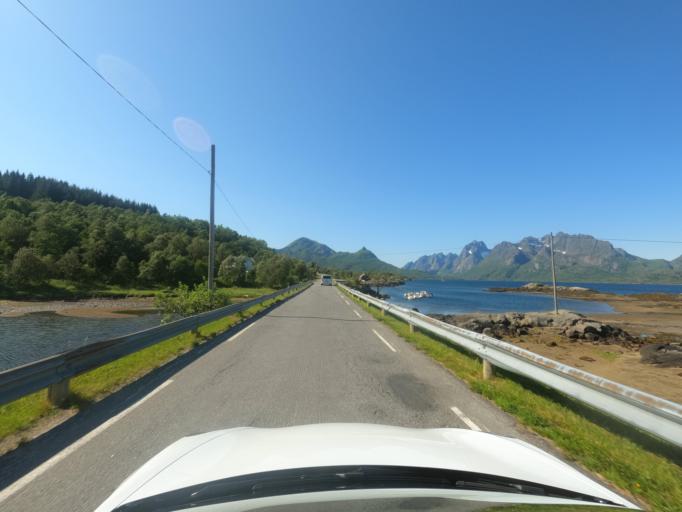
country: NO
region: Nordland
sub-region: Hadsel
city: Stokmarknes
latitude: 68.3193
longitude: 15.0010
